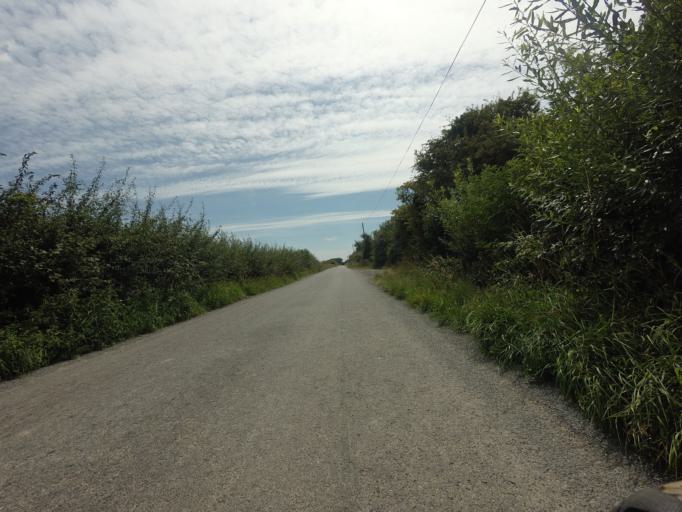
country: GB
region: England
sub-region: Kent
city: Stone
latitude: 51.0041
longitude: 0.7993
